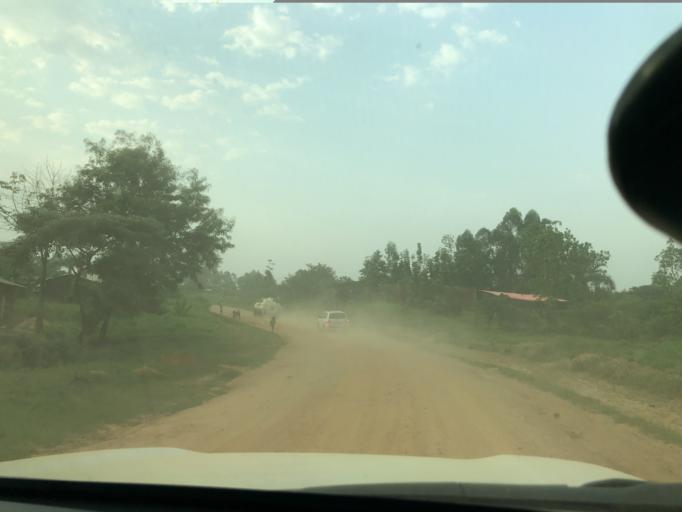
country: UG
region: Western Region
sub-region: Kasese District
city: Margherita
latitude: 0.3397
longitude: 29.6706
